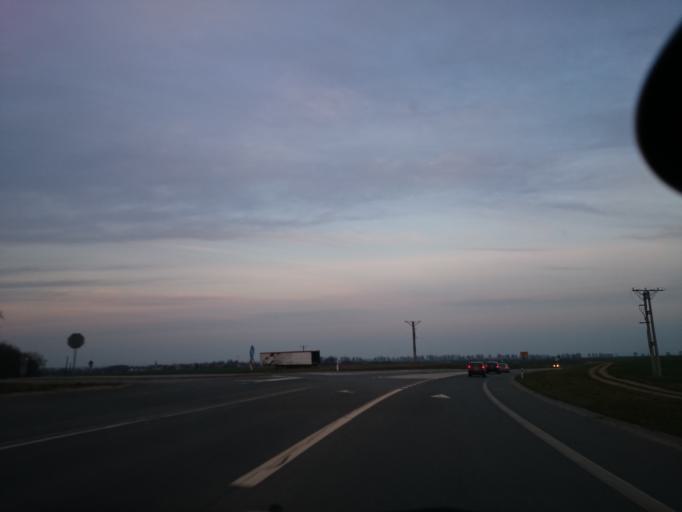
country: PL
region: Opole Voivodeship
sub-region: Powiat prudnicki
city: Biala
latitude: 50.3700
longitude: 17.6541
